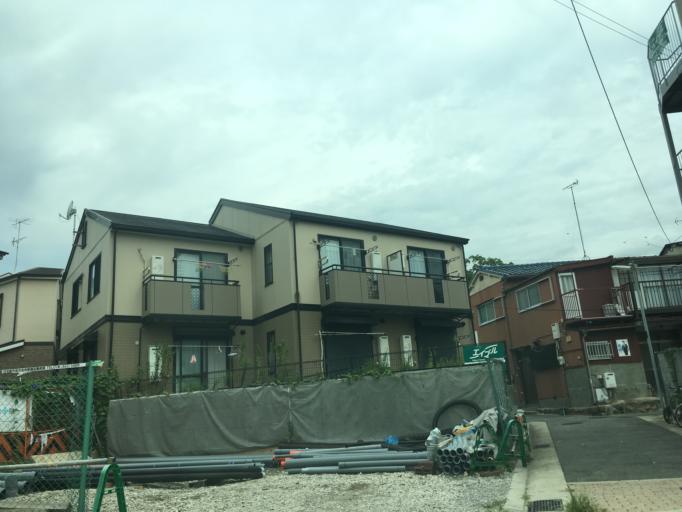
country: JP
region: Hyogo
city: Kobe
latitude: 34.7158
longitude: 135.2334
